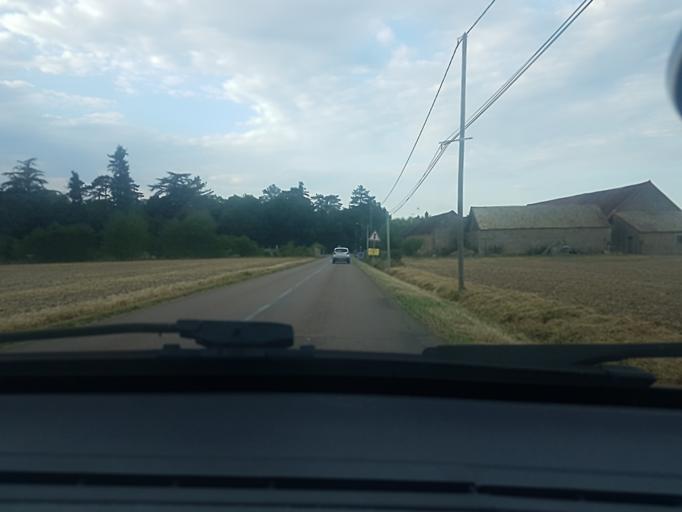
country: FR
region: Bourgogne
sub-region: Departement de Saone-et-Loire
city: Buxy
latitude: 46.7069
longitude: 4.7731
